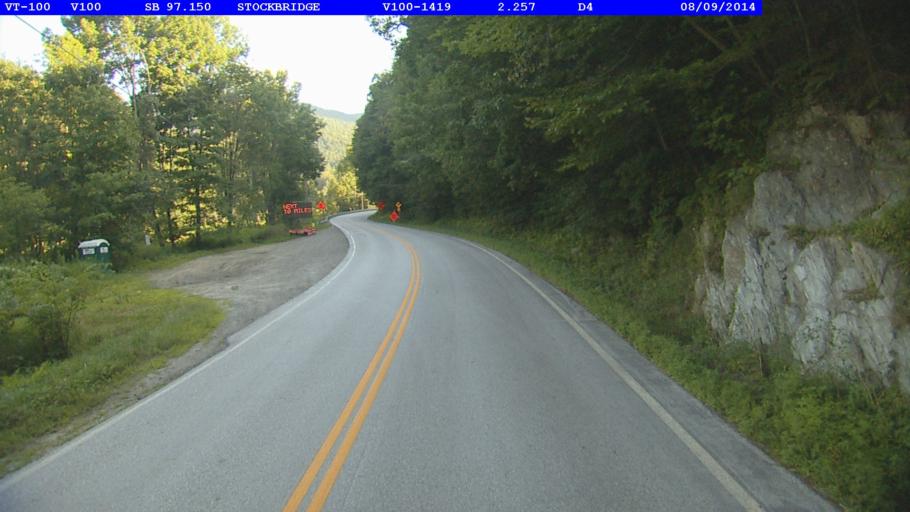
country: US
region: Vermont
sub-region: Orange County
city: Randolph
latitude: 43.7759
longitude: -72.7574
